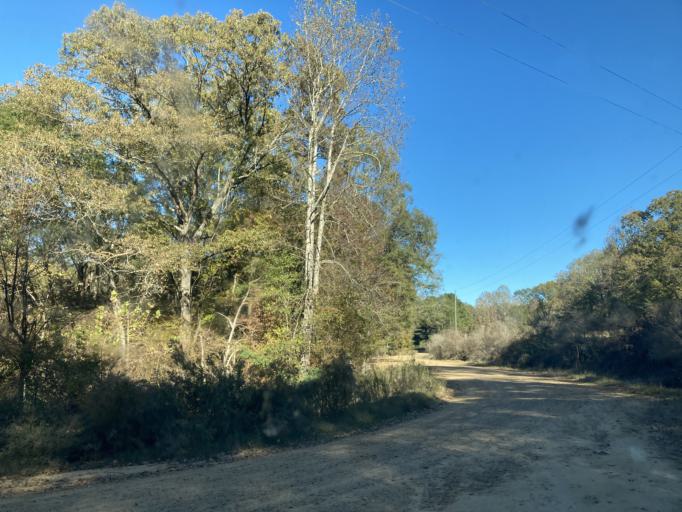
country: US
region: Mississippi
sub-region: Yazoo County
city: Yazoo City
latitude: 32.7437
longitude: -90.4325
